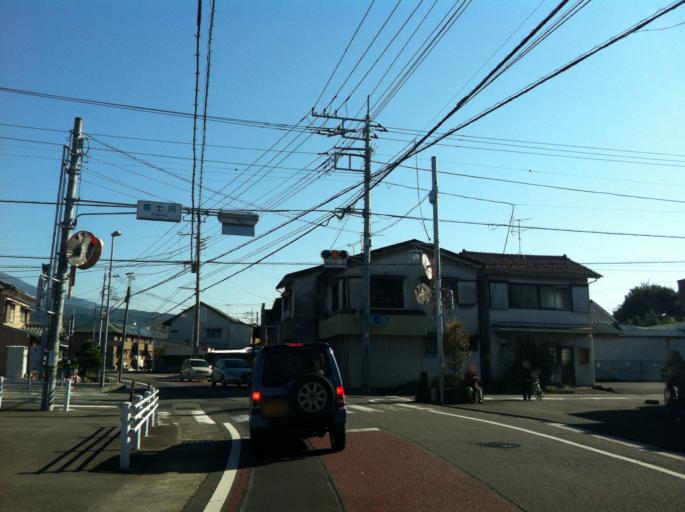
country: JP
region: Shizuoka
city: Fuji
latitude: 35.1648
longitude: 138.7280
